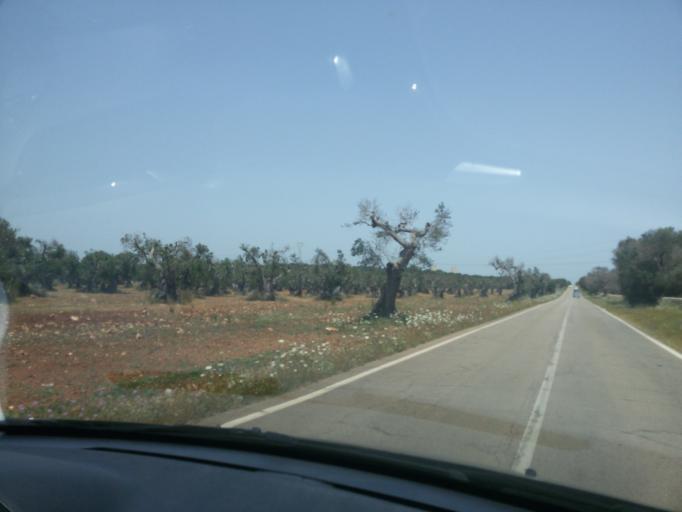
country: IT
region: Apulia
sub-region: Provincia di Lecce
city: Porto Cesareo
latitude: 40.2876
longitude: 17.9112
